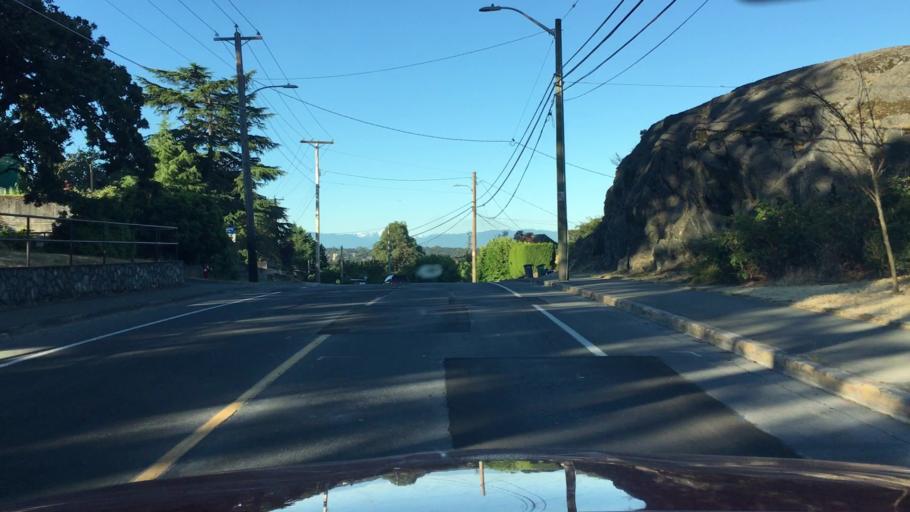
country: CA
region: British Columbia
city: Oak Bay
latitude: 48.4483
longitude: -123.3258
